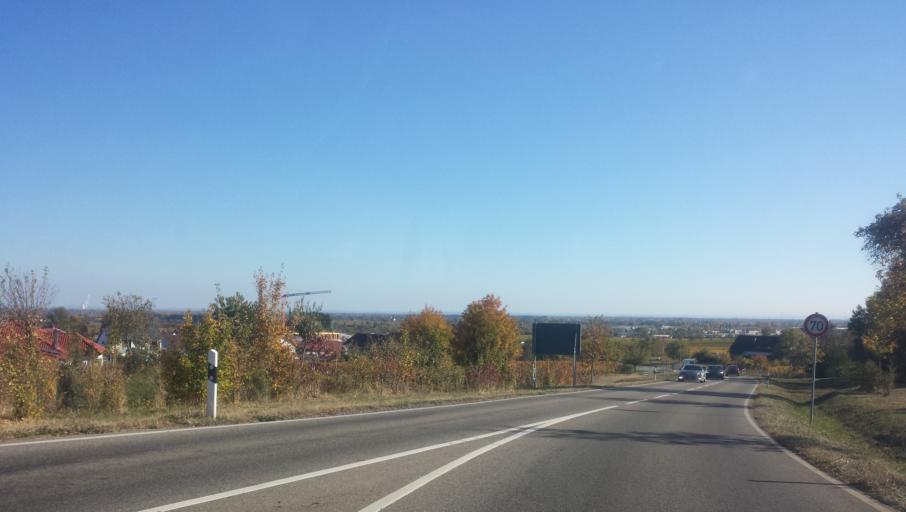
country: DE
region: Rheinland-Pfalz
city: Maikammer
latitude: 49.3014
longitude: 8.1255
